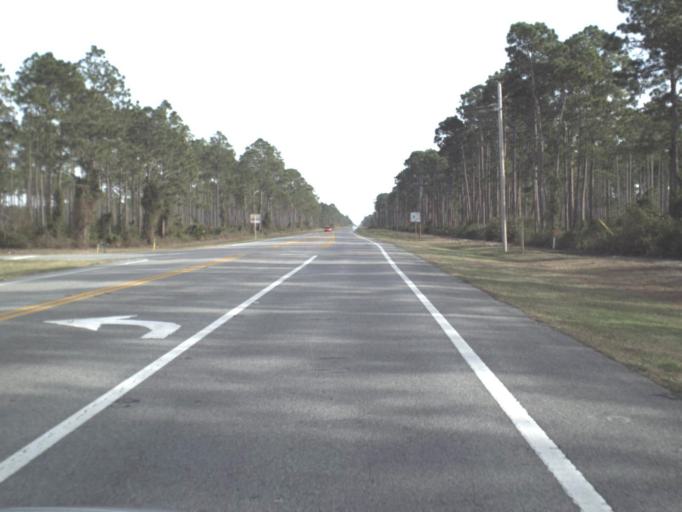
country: US
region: Florida
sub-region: Bay County
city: Tyndall Air Force Base
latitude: 30.0515
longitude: -85.5663
